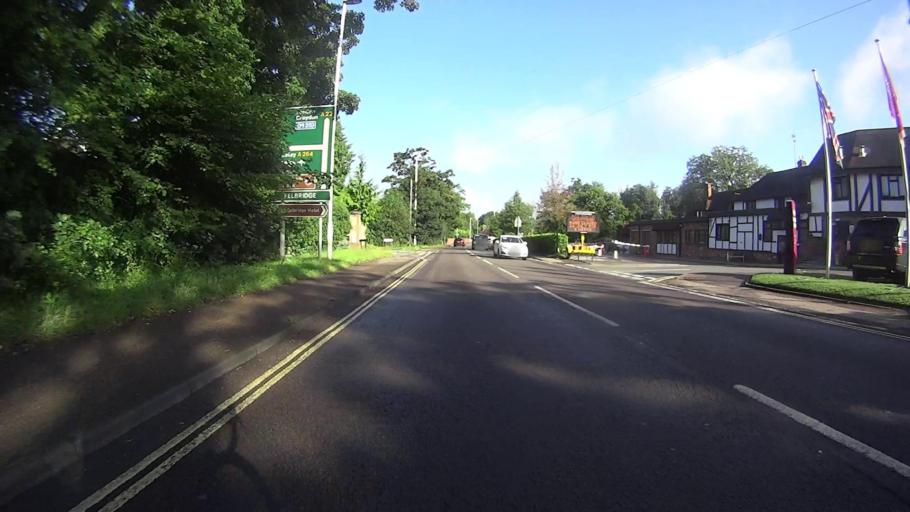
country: GB
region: England
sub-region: Surrey
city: Felbridge
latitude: 51.1383
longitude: -0.0366
